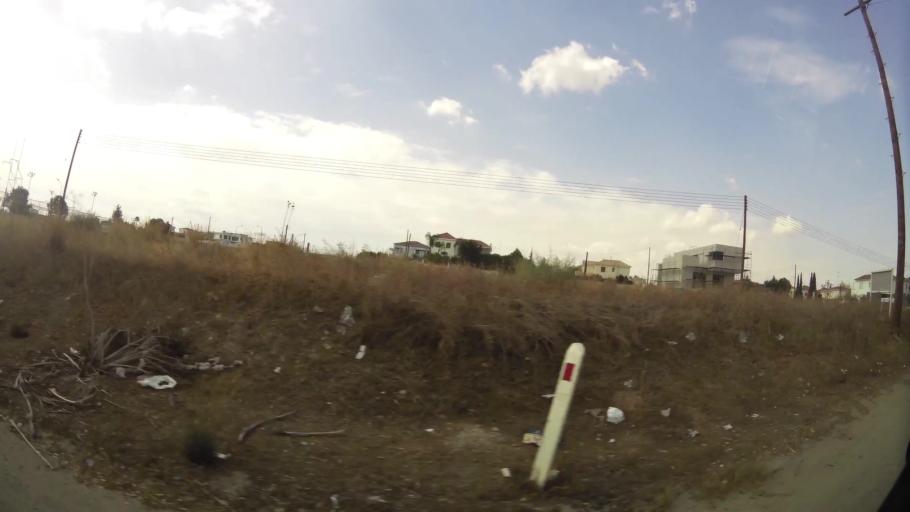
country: CY
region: Lefkosia
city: Tseri
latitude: 35.0975
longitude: 33.3271
